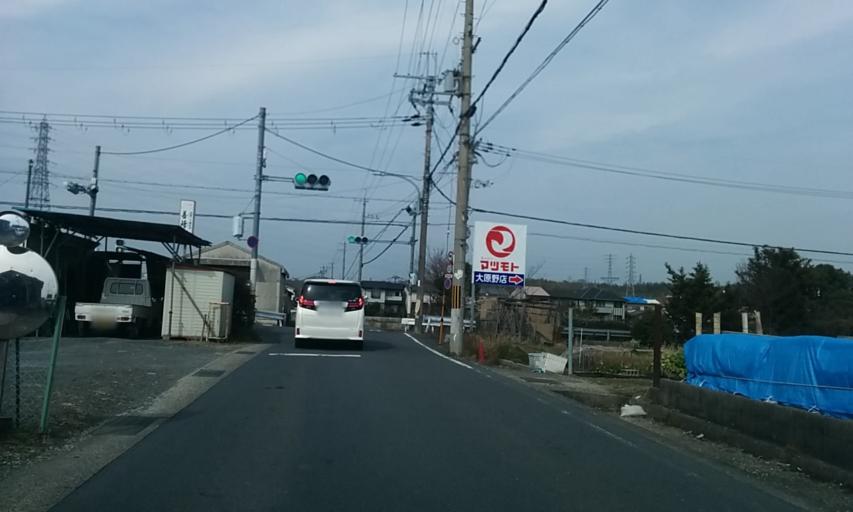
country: JP
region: Kyoto
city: Muko
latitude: 34.9469
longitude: 135.6857
